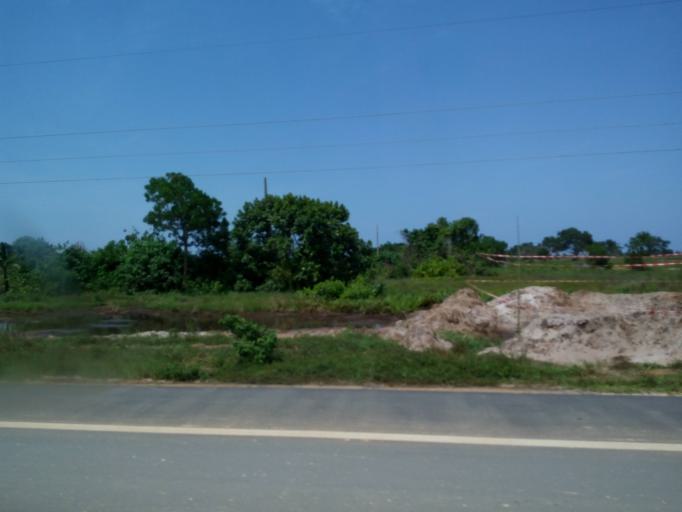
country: CI
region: Sud-Comoe
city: Grand-Bassam
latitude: 5.2304
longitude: -3.7547
